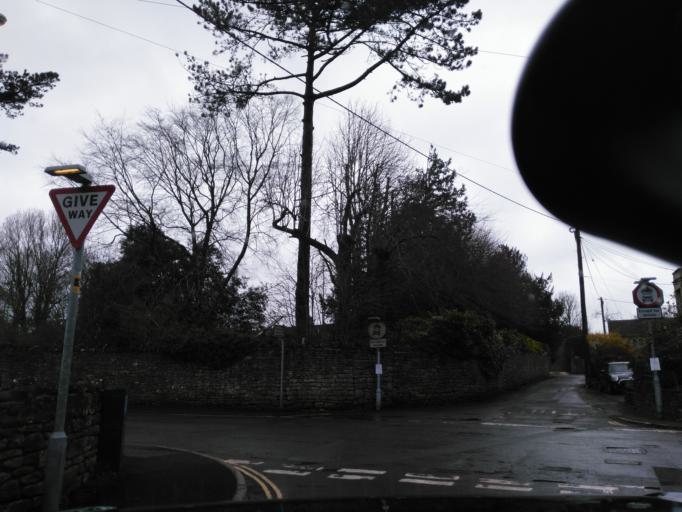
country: GB
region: England
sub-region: Bath and North East Somerset
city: Freshford
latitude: 51.3463
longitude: -2.2922
